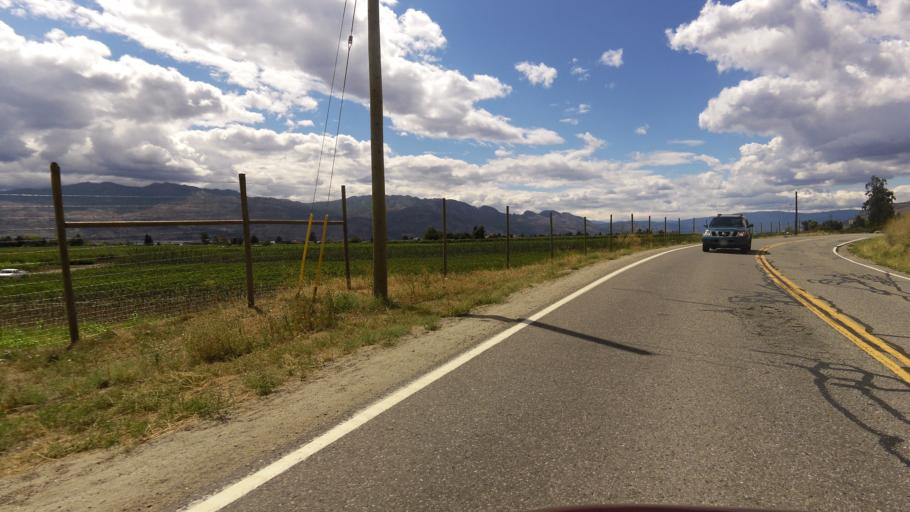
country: CA
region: British Columbia
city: West Kelowna
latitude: 49.8317
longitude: -119.5842
